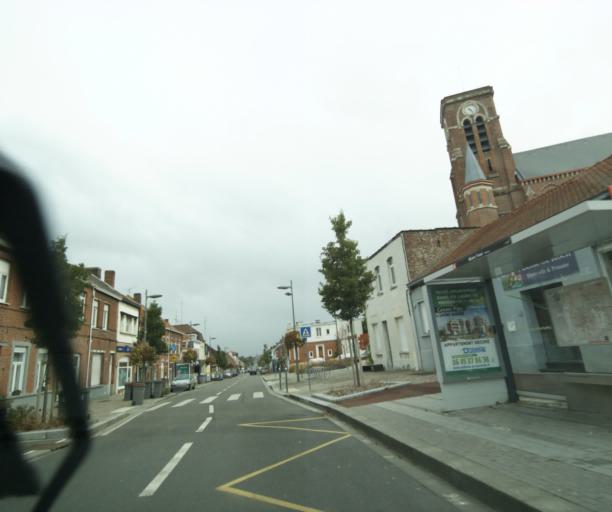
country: FR
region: Nord-Pas-de-Calais
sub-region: Departement du Nord
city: Roncq
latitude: 50.7368
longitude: 3.1156
